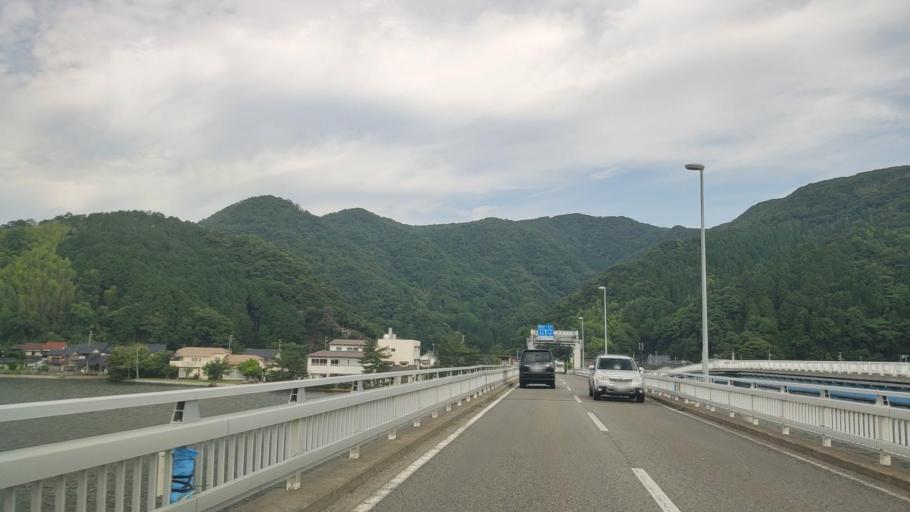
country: JP
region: Hyogo
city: Toyooka
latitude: 35.6415
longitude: 134.8264
